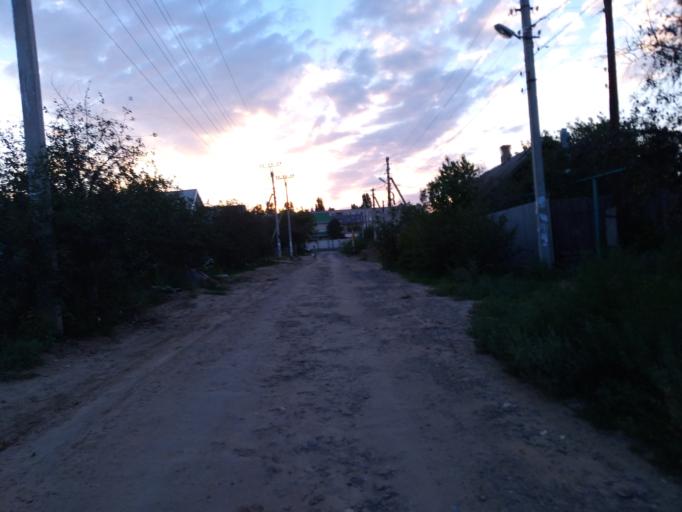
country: RU
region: Volgograd
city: Volgograd
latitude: 48.6699
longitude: 44.4521
